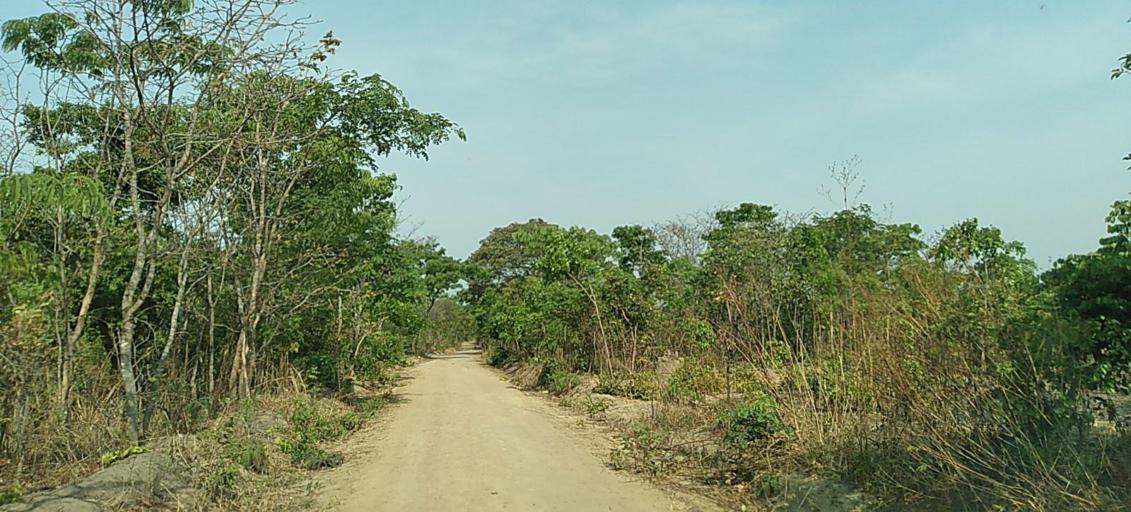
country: ZM
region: Copperbelt
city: Luanshya
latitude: -13.2209
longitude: 28.6655
